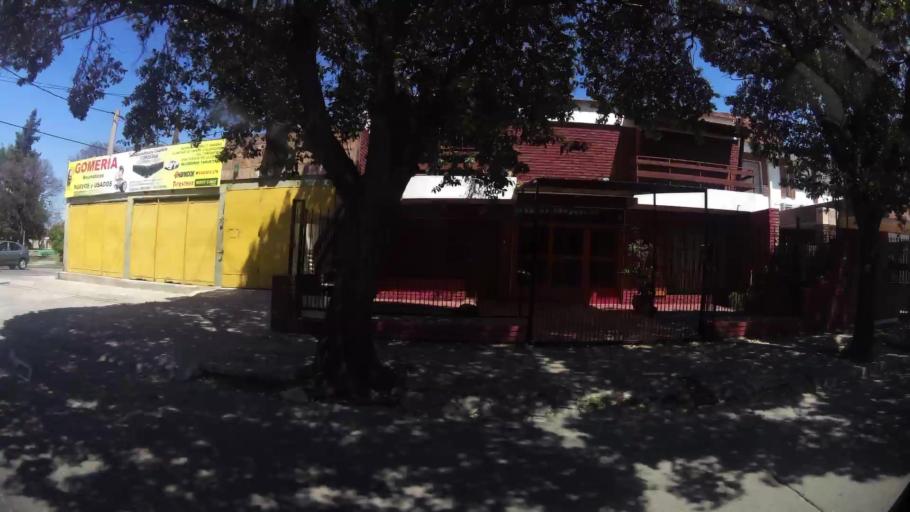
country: AR
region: Cordoba
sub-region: Departamento de Capital
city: Cordoba
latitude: -31.4245
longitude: -64.2096
